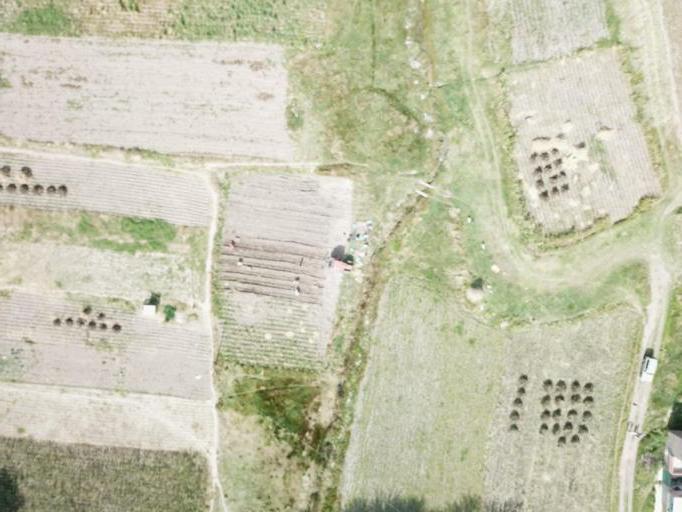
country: BO
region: La Paz
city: Achacachi
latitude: -16.0560
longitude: -68.8124
